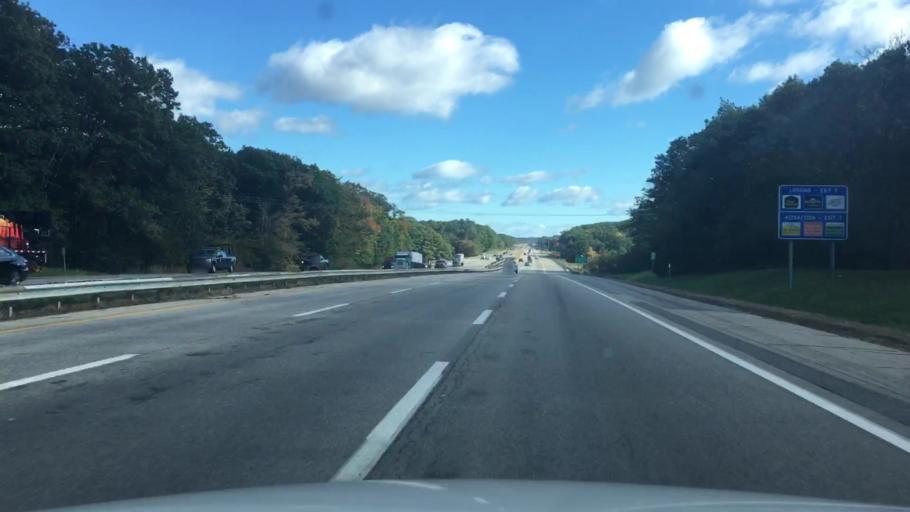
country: US
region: Maine
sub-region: York County
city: York Harbor
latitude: 43.1416
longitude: -70.6974
